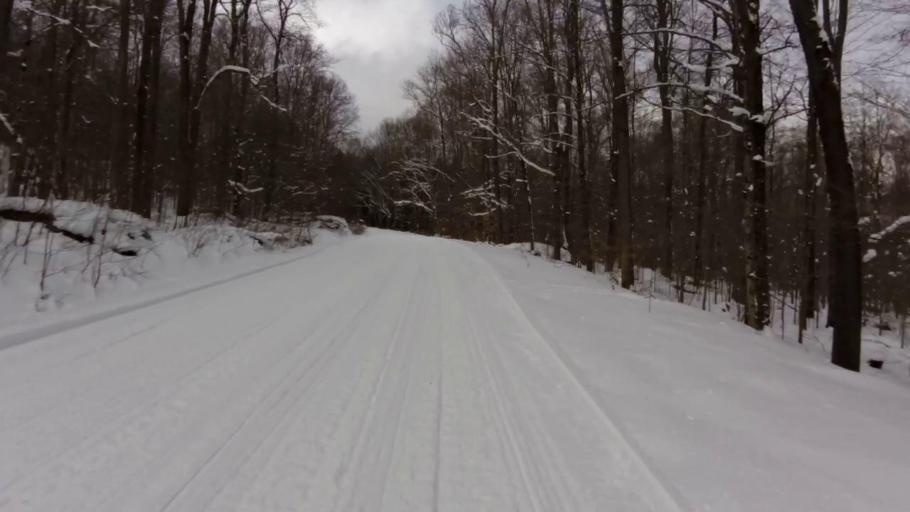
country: US
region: New York
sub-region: Cattaraugus County
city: Salamanca
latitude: 42.0713
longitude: -78.7577
